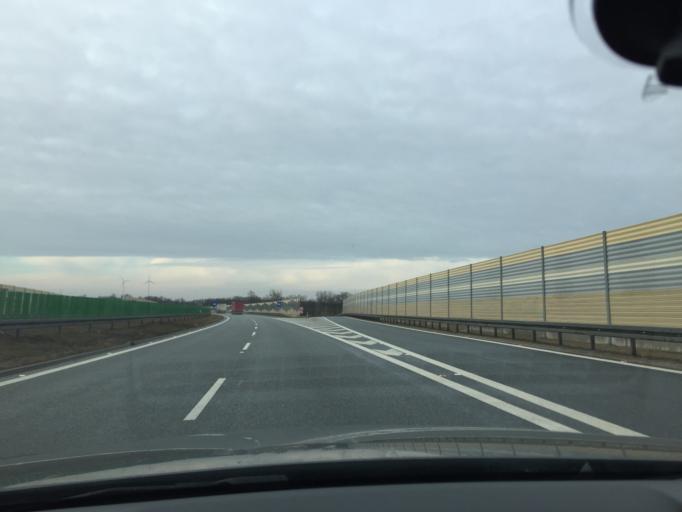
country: PL
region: Masovian Voivodeship
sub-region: Powiat zyrardowski
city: Radziejowice
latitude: 52.0037
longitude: 20.5647
